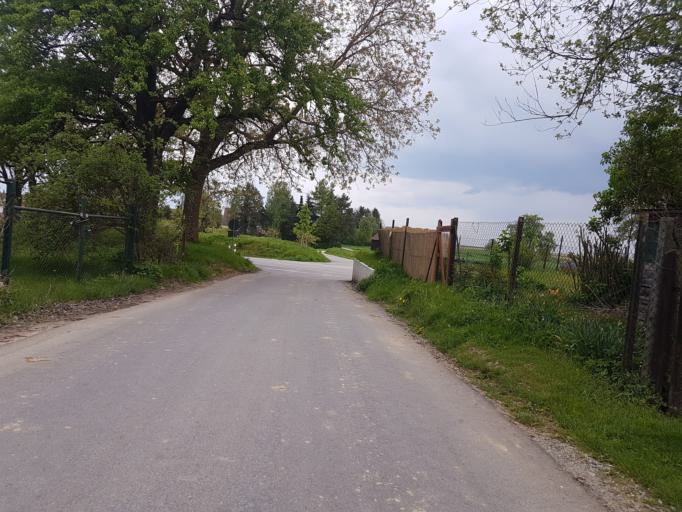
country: DE
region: Baden-Wuerttemberg
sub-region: Regierungsbezirk Stuttgart
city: Bondorf
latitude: 48.5217
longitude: 8.8223
